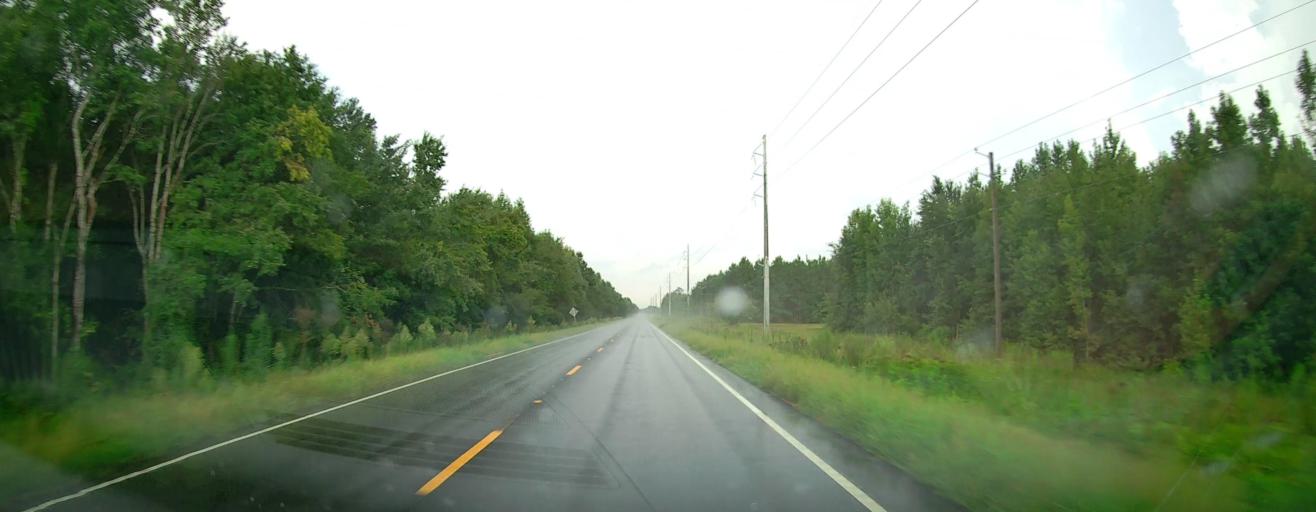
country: US
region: Georgia
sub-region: Dodge County
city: Chester
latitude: 32.5676
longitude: -83.1792
